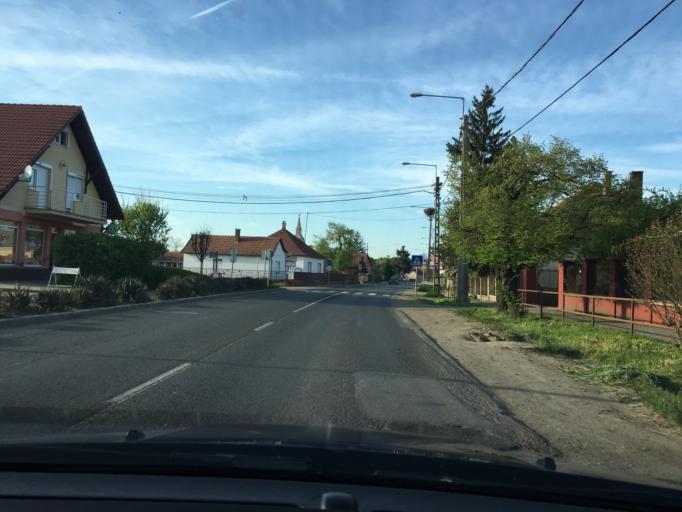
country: HU
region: Hajdu-Bihar
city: Berettyoujfalu
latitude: 47.2009
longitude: 21.5378
